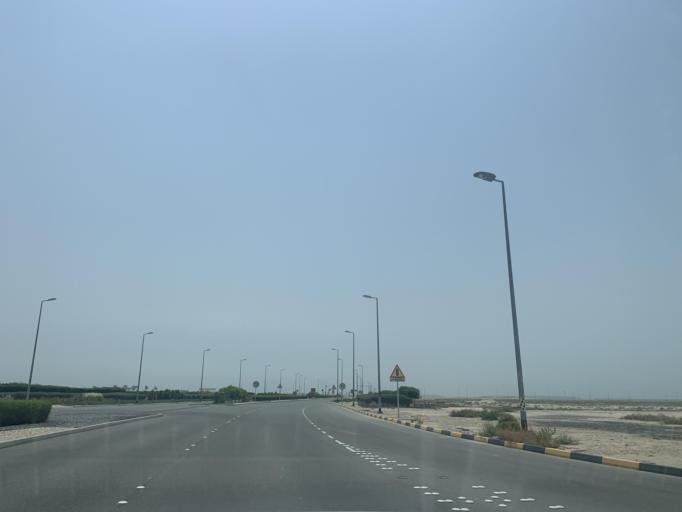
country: BH
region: Central Governorate
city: Dar Kulayb
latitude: 25.8484
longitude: 50.5925
